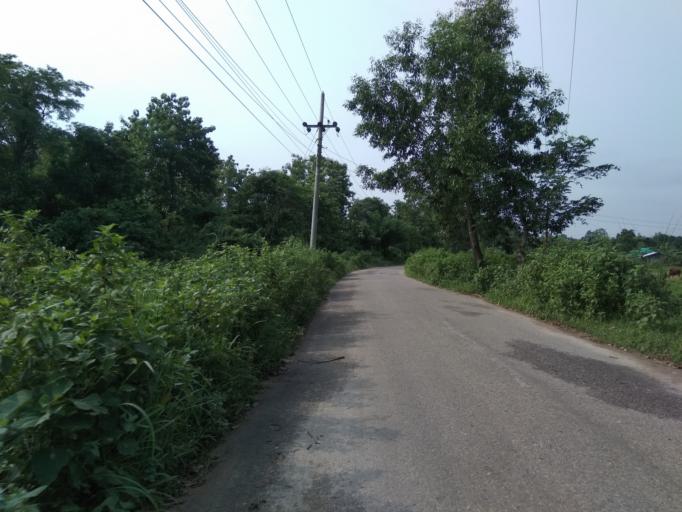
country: BD
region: Chittagong
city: Khagrachhari
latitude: 23.0272
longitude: 92.0145
